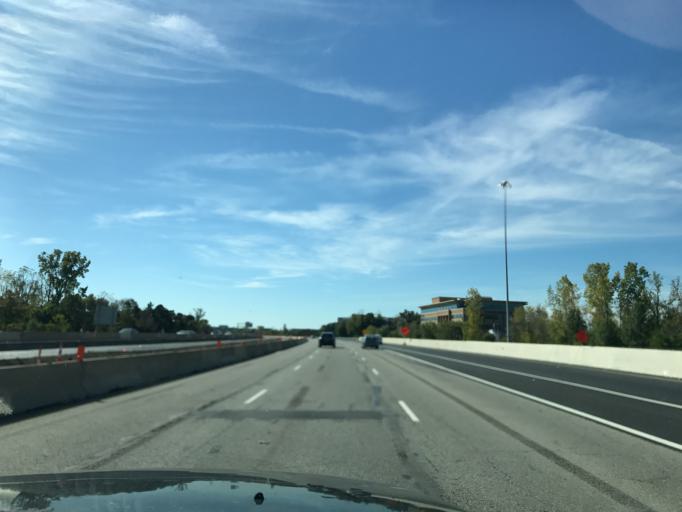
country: US
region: Ohio
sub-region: Franklin County
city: Dublin
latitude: 40.0929
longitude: -83.1380
